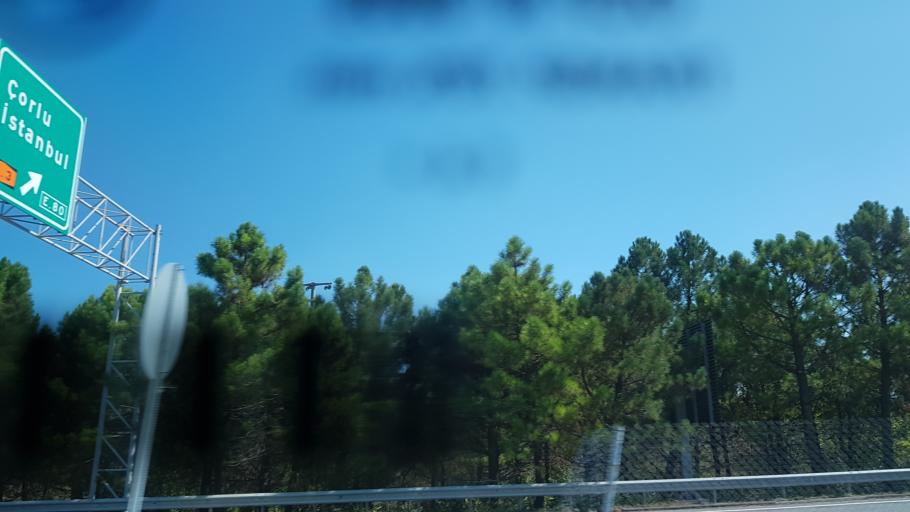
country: TR
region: Kirklareli
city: Luleburgaz
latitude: 41.4461
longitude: 27.3890
